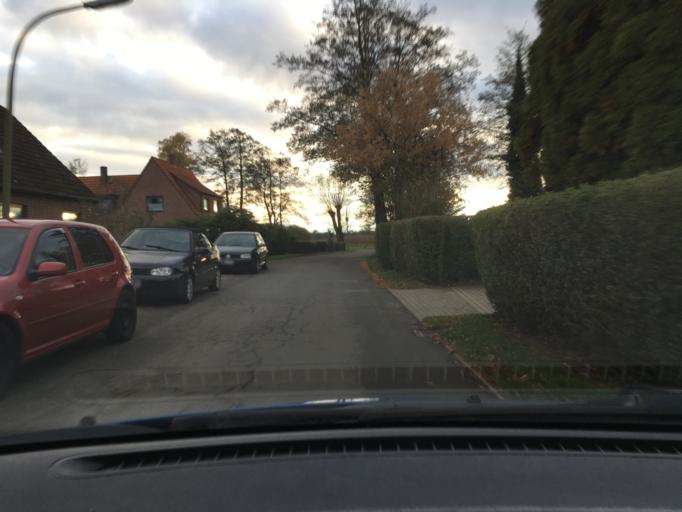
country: DE
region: Hamburg
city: Harburg
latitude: 53.4571
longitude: 10.0420
